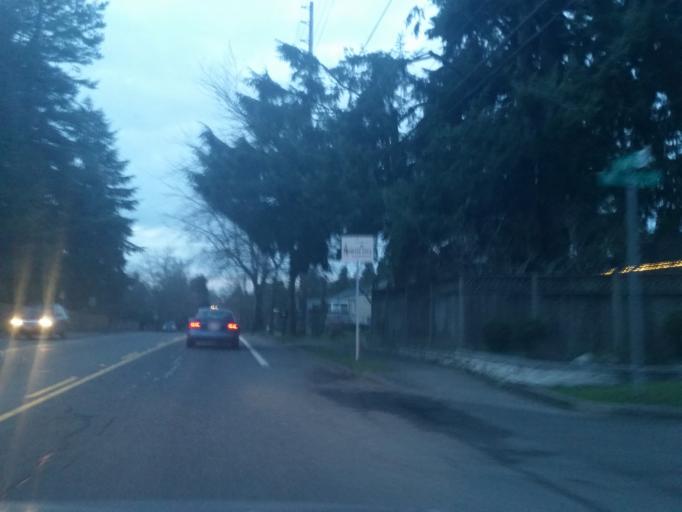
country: US
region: Washington
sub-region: King County
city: Shoreline
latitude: 47.7493
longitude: -122.3132
